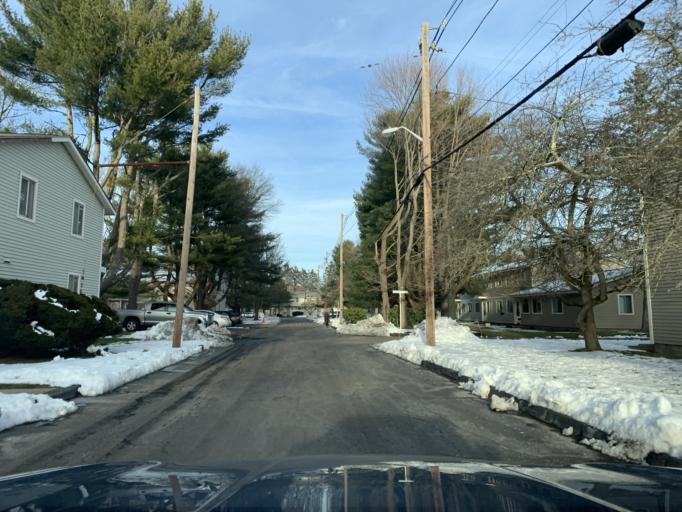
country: US
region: Rhode Island
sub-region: Washington County
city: North Kingstown
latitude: 41.5949
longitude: -71.4408
